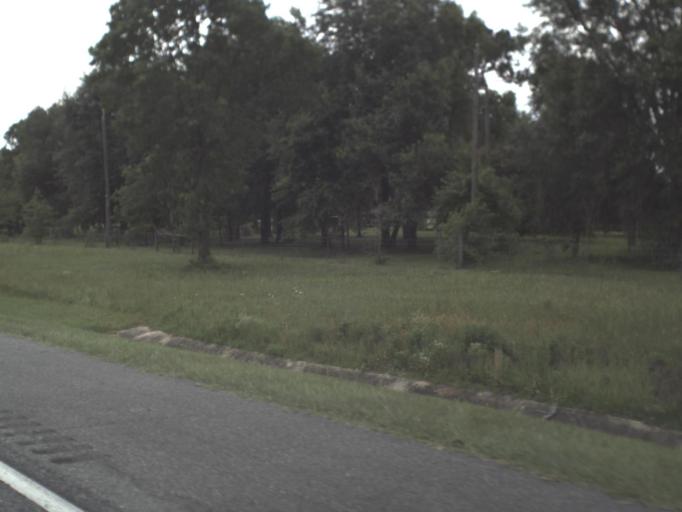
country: US
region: Florida
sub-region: Columbia County
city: Five Points
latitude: 30.2237
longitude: -82.7162
